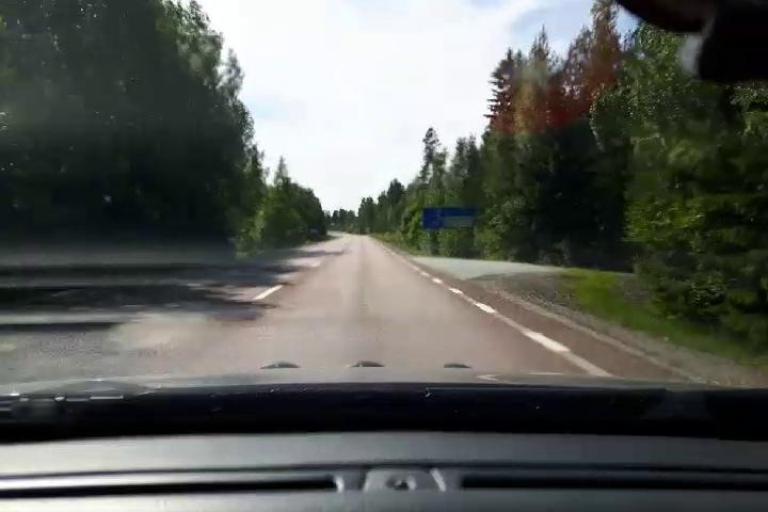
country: SE
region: Gaevleborg
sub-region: Bollnas Kommun
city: Kilafors
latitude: 61.2189
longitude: 16.6914
